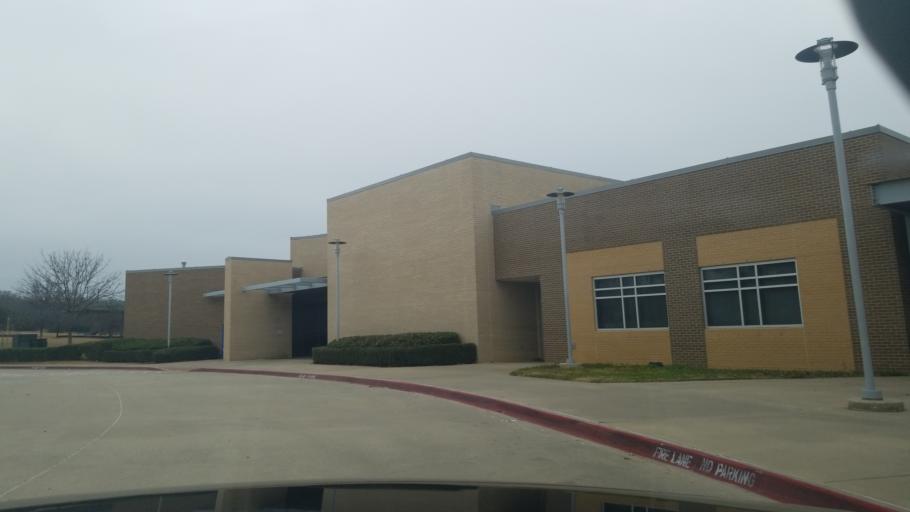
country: US
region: Texas
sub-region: Denton County
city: Corinth
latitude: 33.1704
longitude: -97.0668
